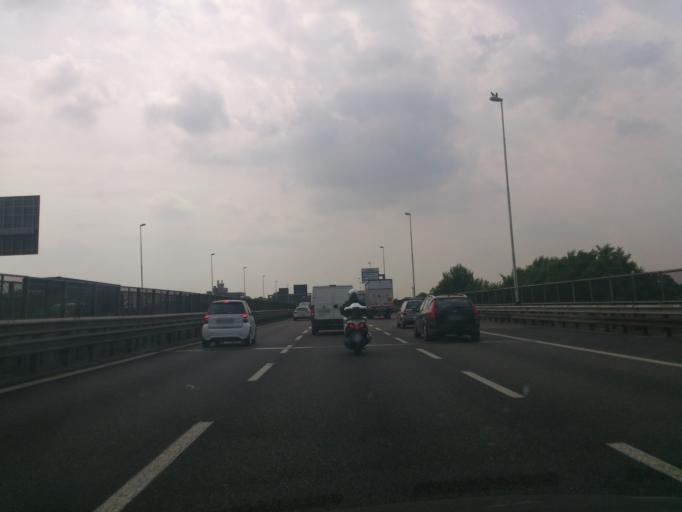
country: IT
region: Lombardy
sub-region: Citta metropolitana di Milano
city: Novegro-Tregarezzo-San Felice
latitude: 45.4805
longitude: 9.2521
